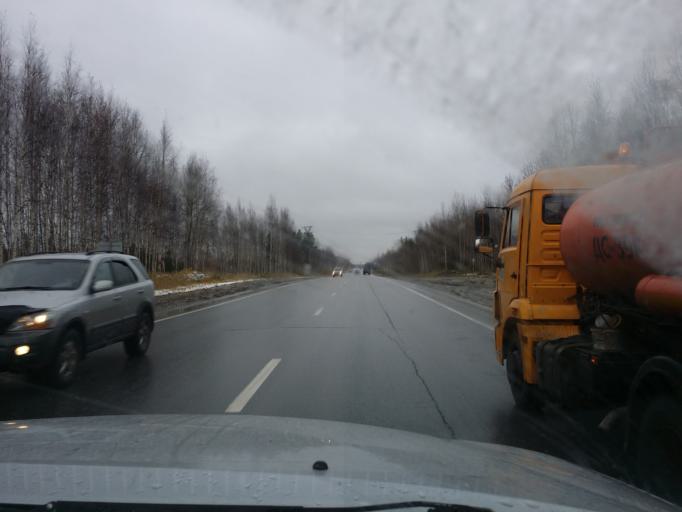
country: RU
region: Khanty-Mansiyskiy Avtonomnyy Okrug
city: Megion
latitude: 61.0651
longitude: 76.1155
